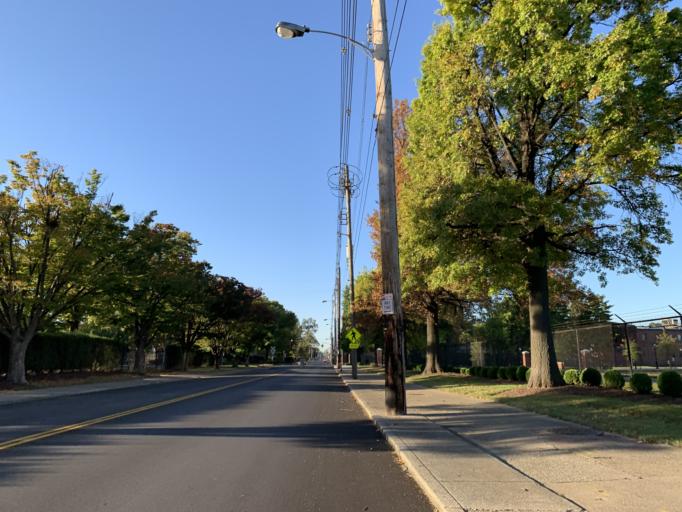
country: US
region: Kentucky
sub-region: Jefferson County
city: Louisville
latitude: 38.2465
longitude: -85.7831
